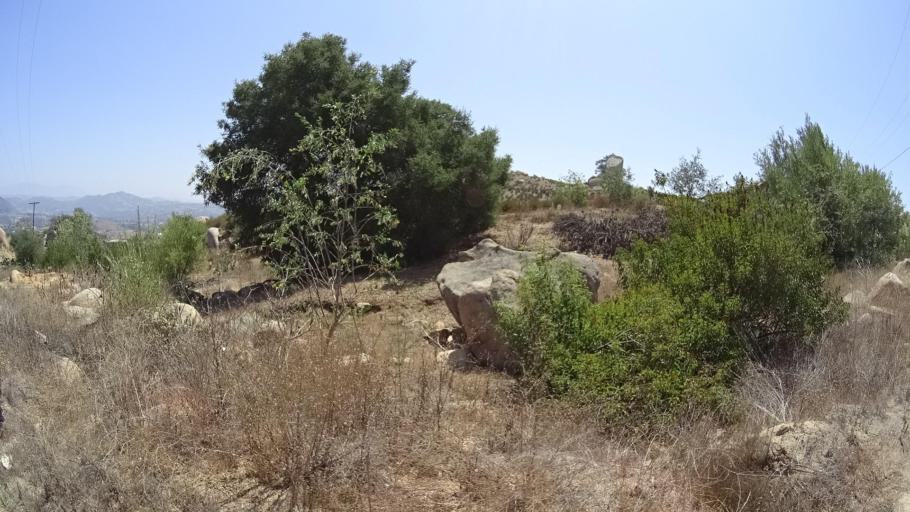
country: US
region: California
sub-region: San Diego County
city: Fallbrook
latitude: 33.4292
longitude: -117.2596
